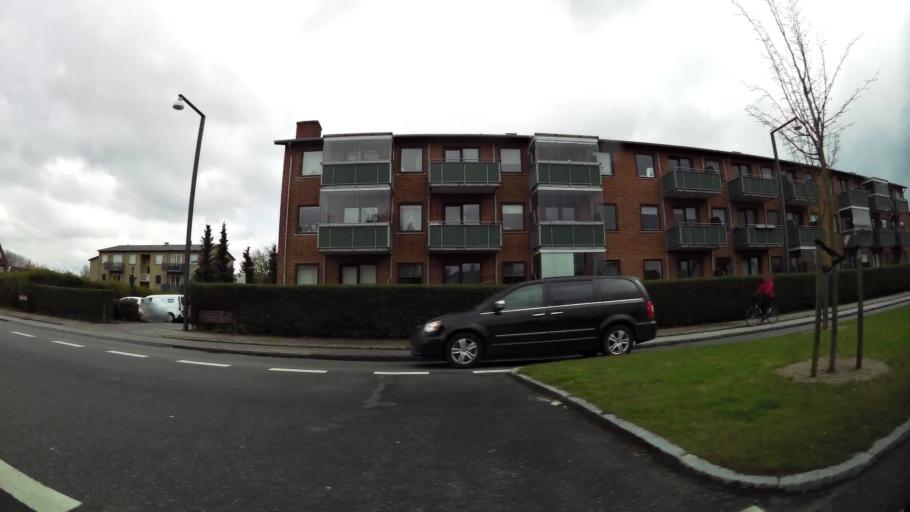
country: DK
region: Capital Region
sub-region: Rodovre Kommune
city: Rodovre
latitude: 55.6864
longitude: 12.4644
